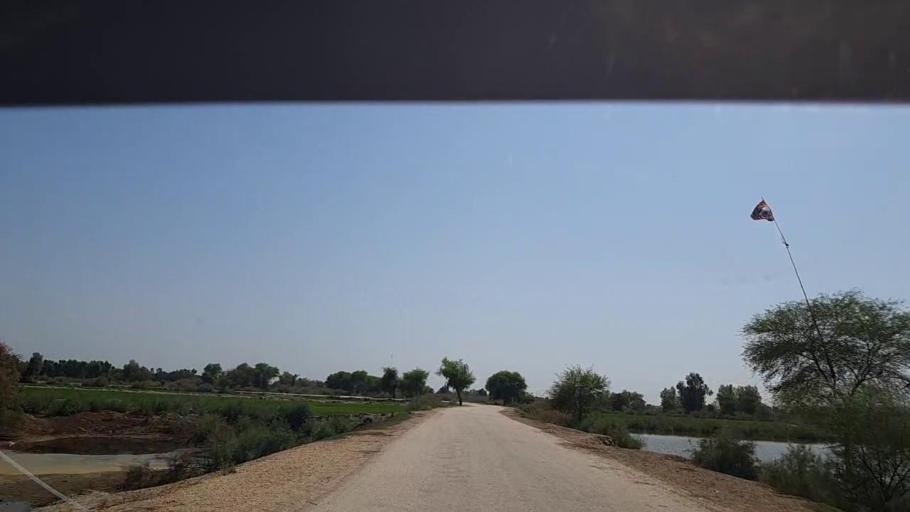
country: PK
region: Sindh
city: Ghauspur
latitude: 28.1593
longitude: 69.1603
